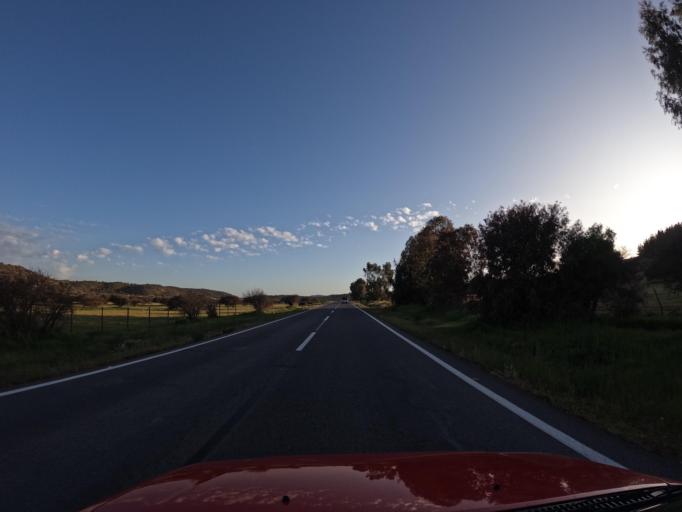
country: CL
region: O'Higgins
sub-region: Provincia de Colchagua
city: Santa Cruz
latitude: -34.3022
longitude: -71.7348
